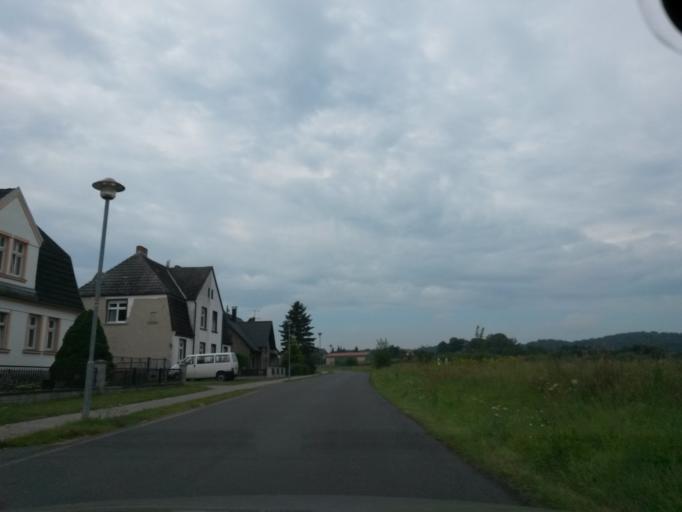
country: DE
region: Brandenburg
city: Chorin
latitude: 52.9018
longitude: 13.8784
